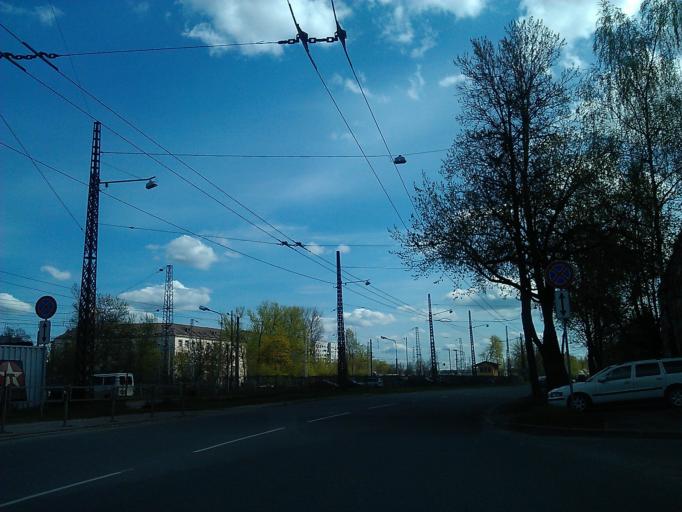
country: LV
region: Riga
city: Riga
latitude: 56.9322
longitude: 24.1689
